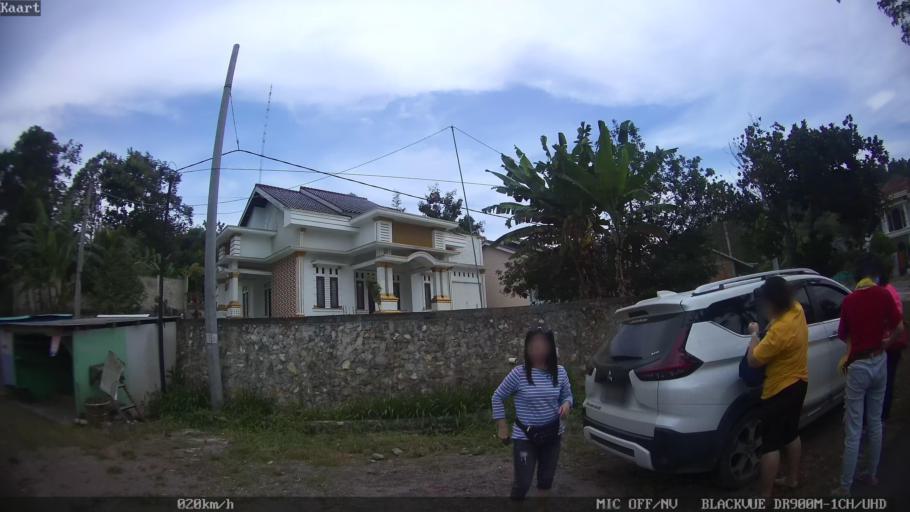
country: ID
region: Lampung
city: Kedaton
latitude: -5.3998
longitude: 105.1911
